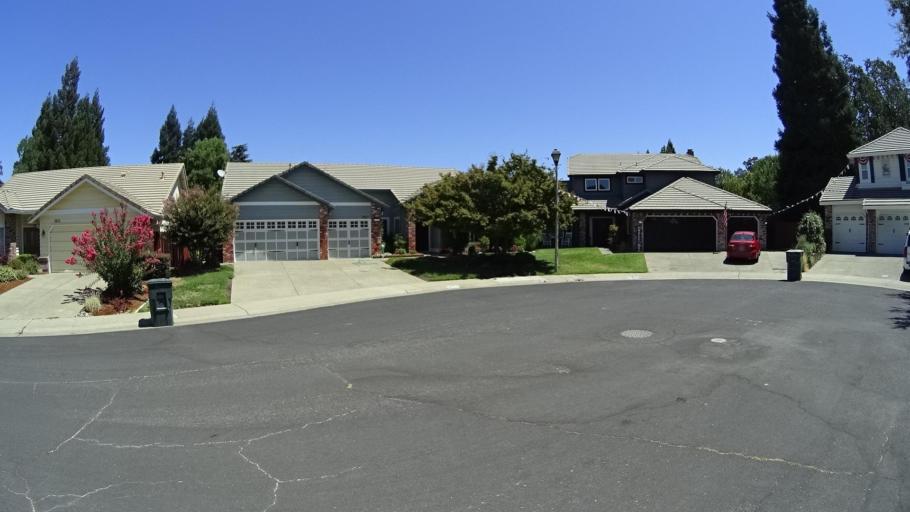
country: US
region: California
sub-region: Placer County
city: Rocklin
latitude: 38.8069
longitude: -121.2705
